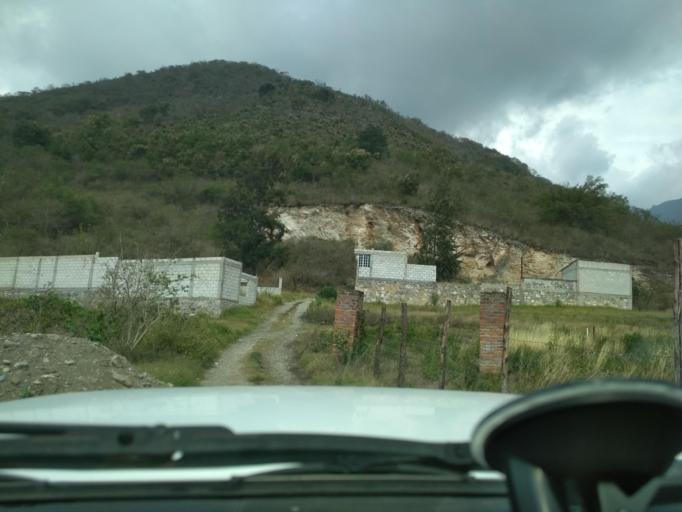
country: MX
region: Veracruz
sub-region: Nogales
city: Taza de Agua Ojo Zarco
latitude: 18.7850
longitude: -97.1969
